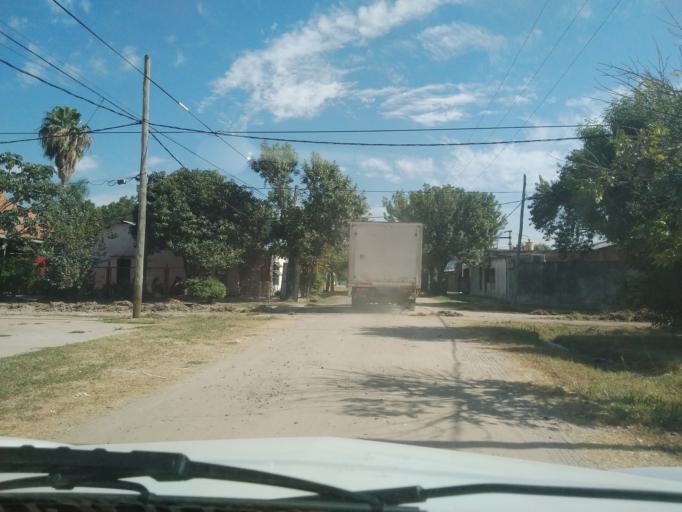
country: AR
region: Corrientes
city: Corrientes
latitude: -27.5121
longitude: -58.7999
